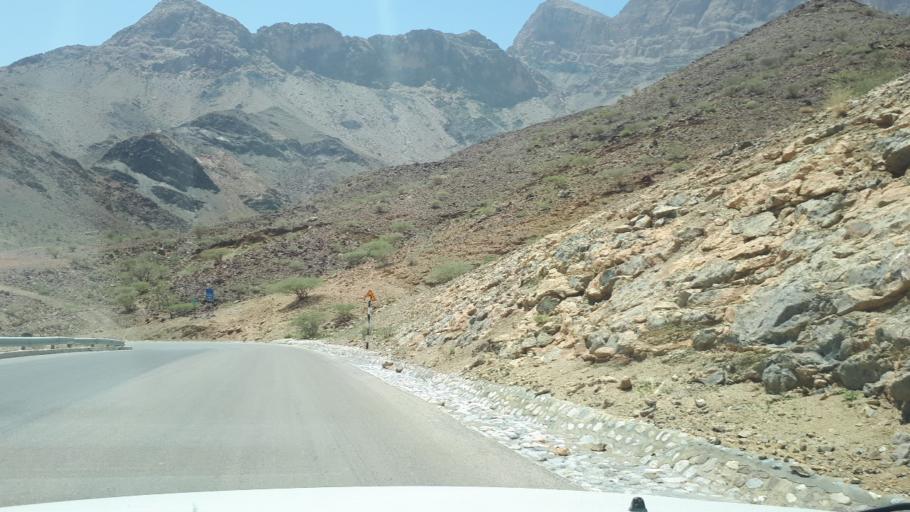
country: OM
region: Muhafazat ad Dakhiliyah
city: Bahla'
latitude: 23.1833
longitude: 57.1404
